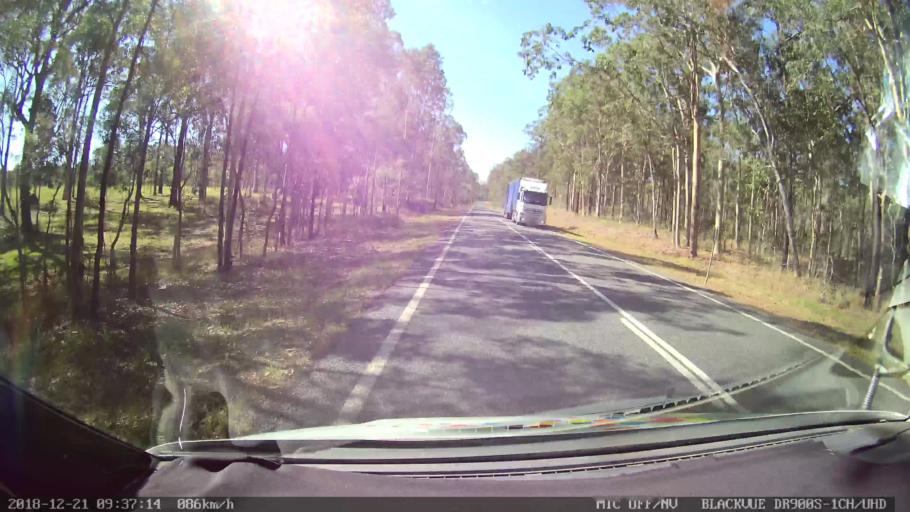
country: AU
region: New South Wales
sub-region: Clarence Valley
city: Grafton
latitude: -29.5336
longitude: 152.9859
